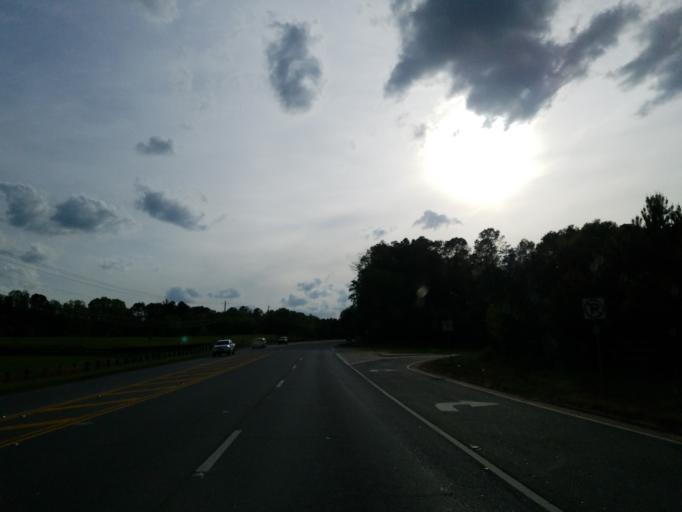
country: US
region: Georgia
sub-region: Cherokee County
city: Ball Ground
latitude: 34.2562
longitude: -84.3310
